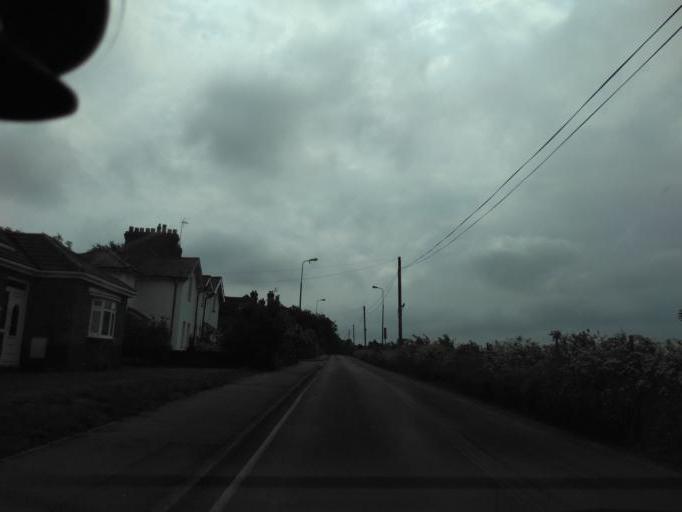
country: GB
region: England
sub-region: Kent
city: Chartham
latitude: 51.2477
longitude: 1.0217
